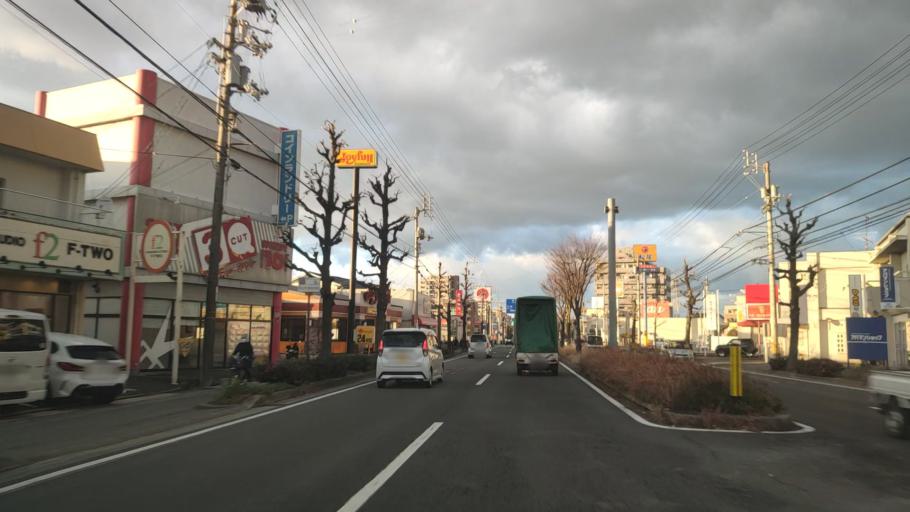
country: JP
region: Ehime
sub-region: Shikoku-chuo Shi
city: Matsuyama
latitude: 33.8106
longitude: 132.7795
